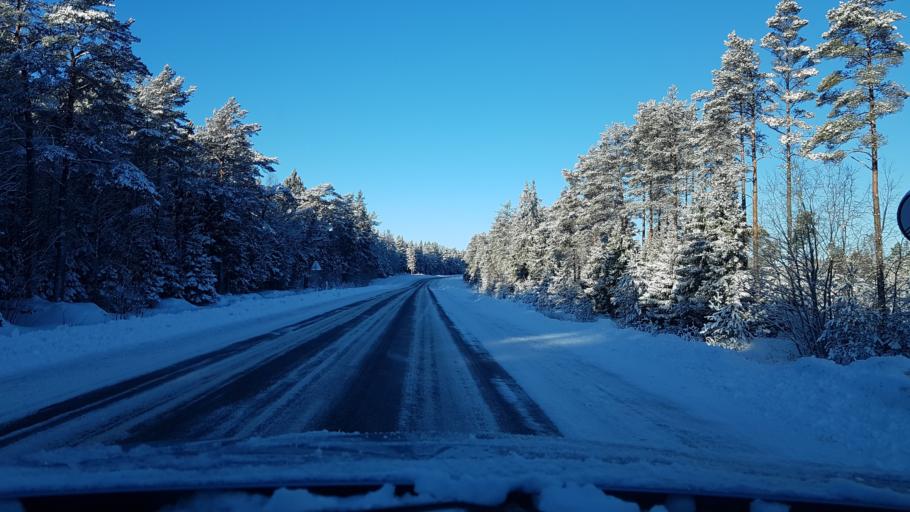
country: EE
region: Hiiumaa
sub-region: Kaerdla linn
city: Kardla
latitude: 58.9638
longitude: 22.8403
